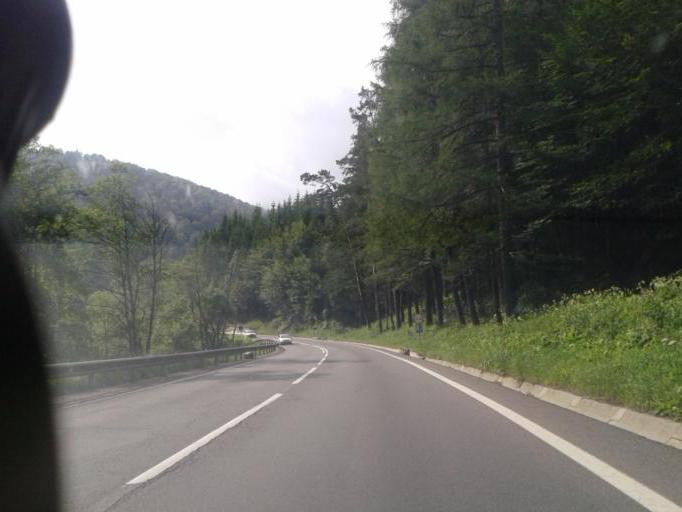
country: RO
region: Prahova
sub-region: Oras Azuga
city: Azuga
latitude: 45.4648
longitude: 25.5636
